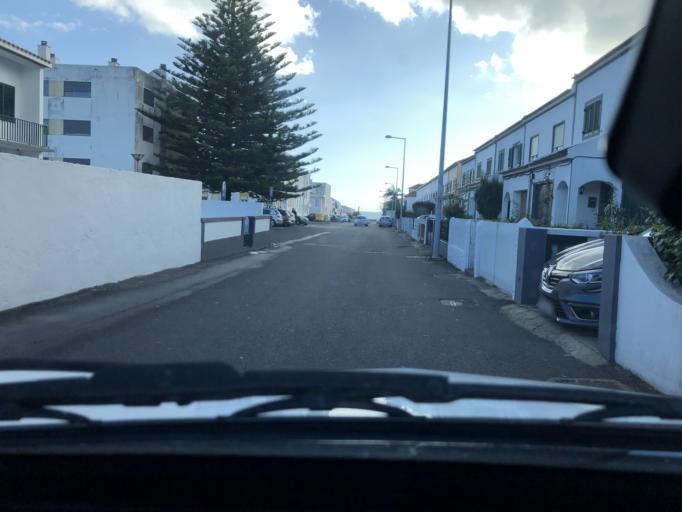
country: PT
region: Azores
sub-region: Ponta Delgada
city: Rosto de Cao
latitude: 37.7469
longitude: -25.6544
